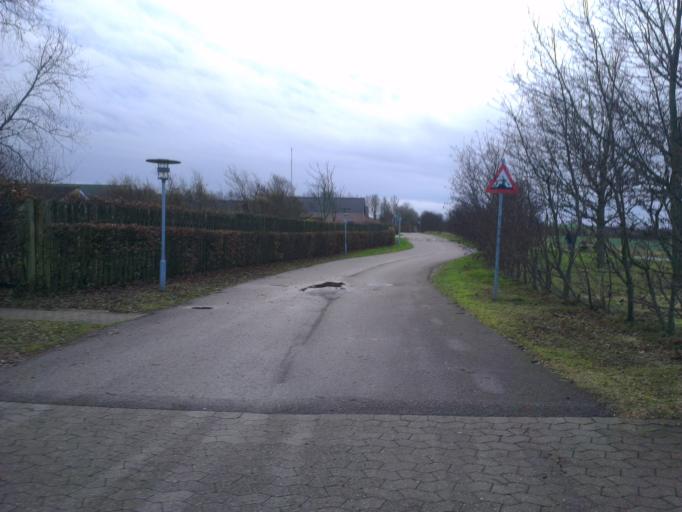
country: DK
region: Capital Region
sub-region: Frederikssund Kommune
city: Jaegerspris
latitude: 55.8512
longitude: 11.9841
